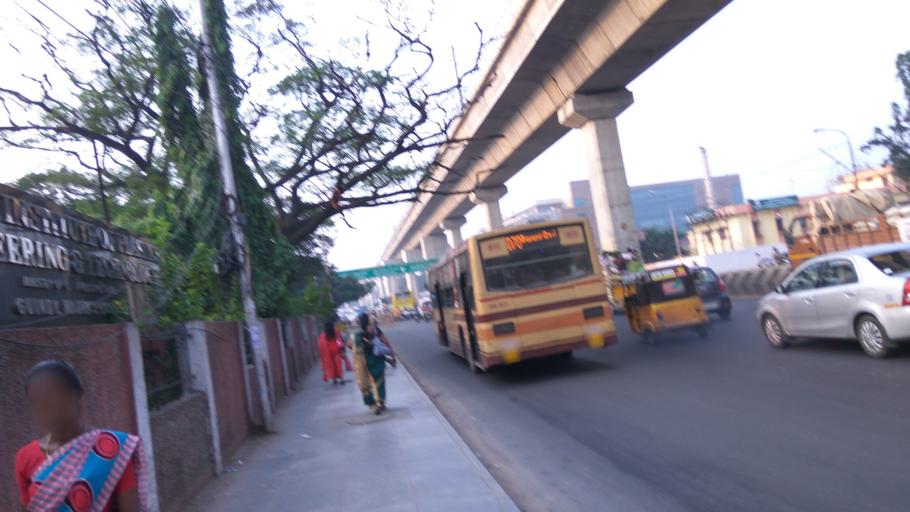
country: IN
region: Tamil Nadu
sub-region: Kancheepuram
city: Alandur
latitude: 13.0141
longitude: 80.2046
